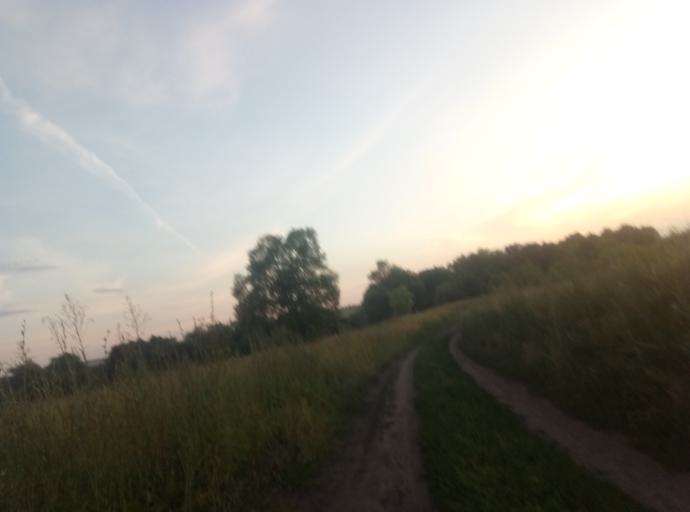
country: RU
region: Tula
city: Kireyevsk
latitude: 53.7986
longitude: 37.8665
